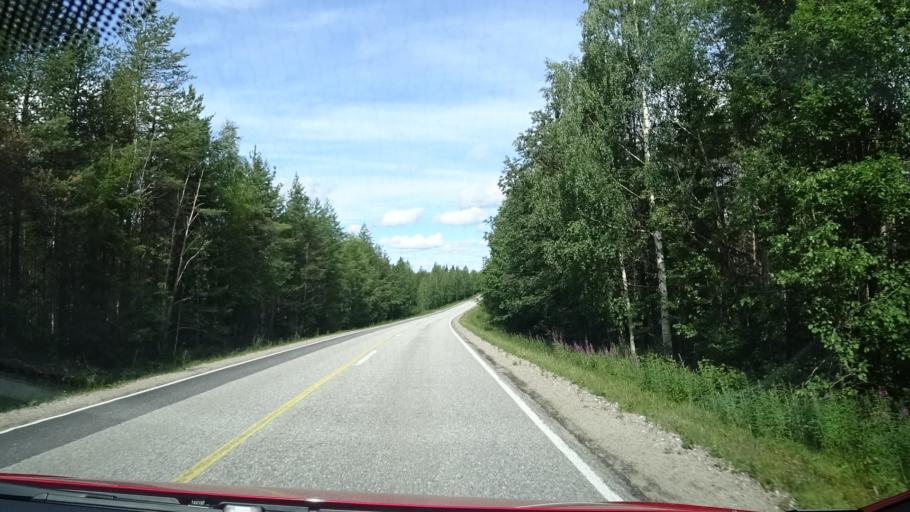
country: FI
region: Kainuu
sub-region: Kehys-Kainuu
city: Kuhmo
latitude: 64.4426
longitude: 29.8002
